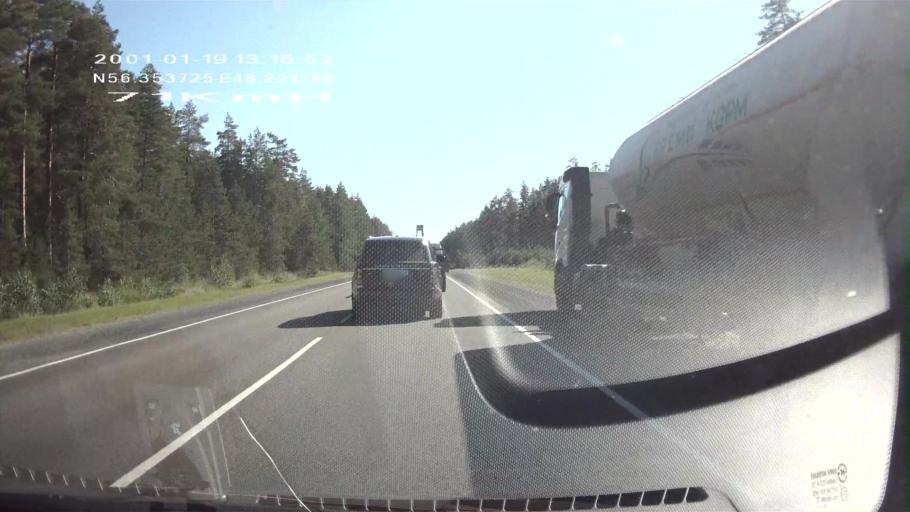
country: RU
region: Mariy-El
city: Suslonger
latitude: 56.3535
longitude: 48.2220
